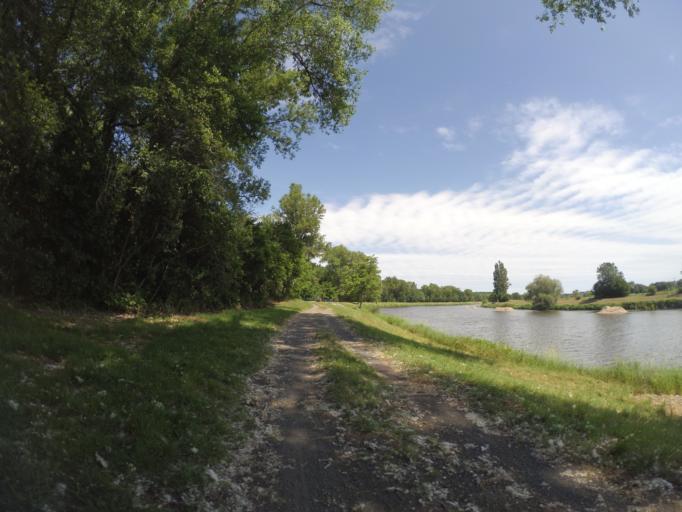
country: CZ
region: Central Bohemia
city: Poricany
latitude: 50.1719
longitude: 14.9275
